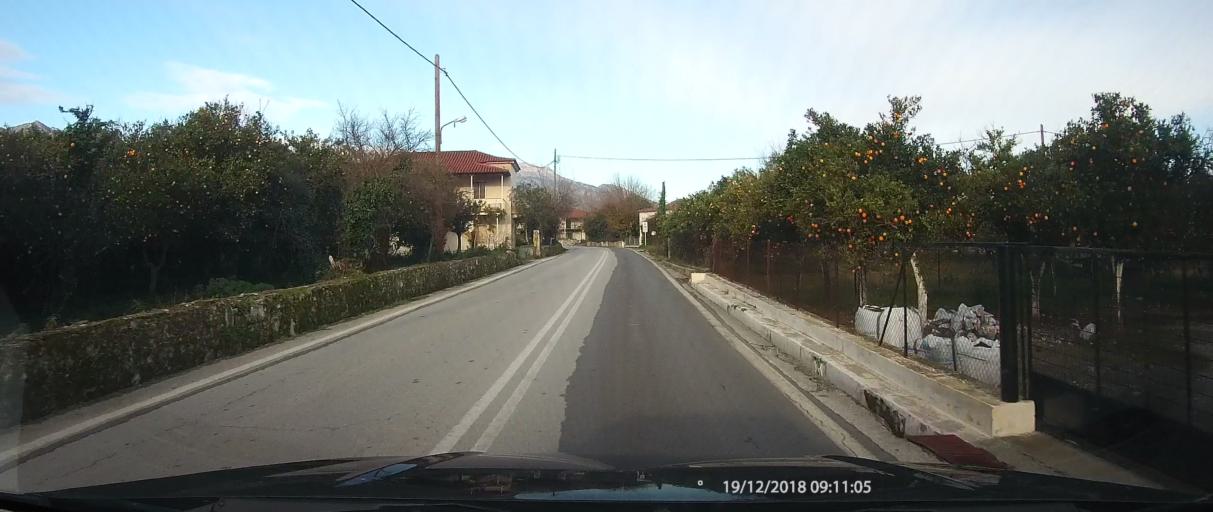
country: GR
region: Peloponnese
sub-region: Nomos Lakonias
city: Sparti
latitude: 37.0778
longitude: 22.4179
